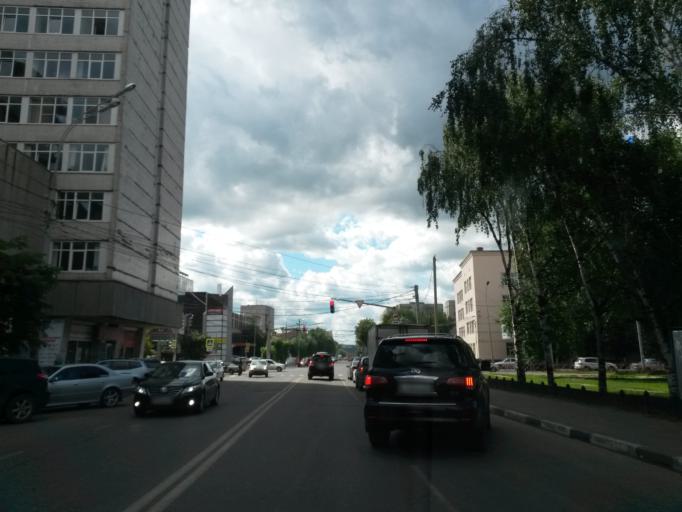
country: RU
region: Jaroslavl
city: Yaroslavl
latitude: 57.6276
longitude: 39.8487
